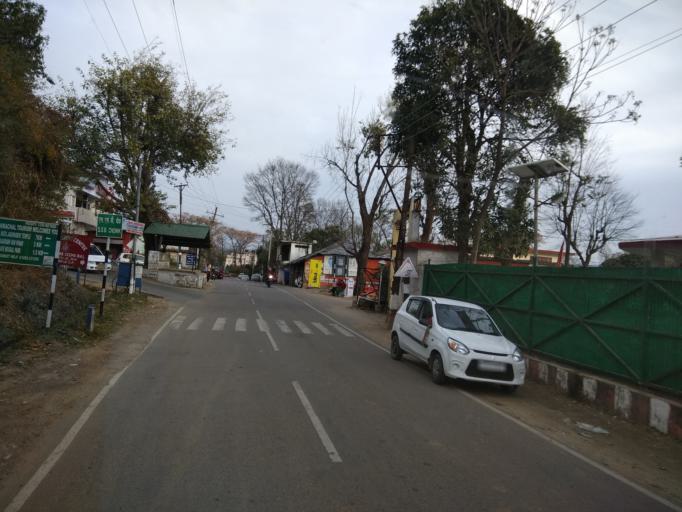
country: IN
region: Himachal Pradesh
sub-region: Kangra
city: Palampur
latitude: 32.1138
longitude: 76.5225
